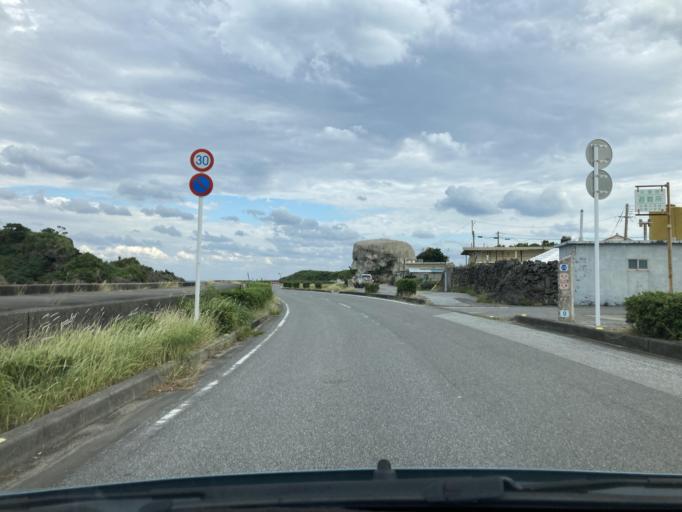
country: JP
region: Okinawa
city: Katsuren-haebaru
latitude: 26.3240
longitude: 127.9645
